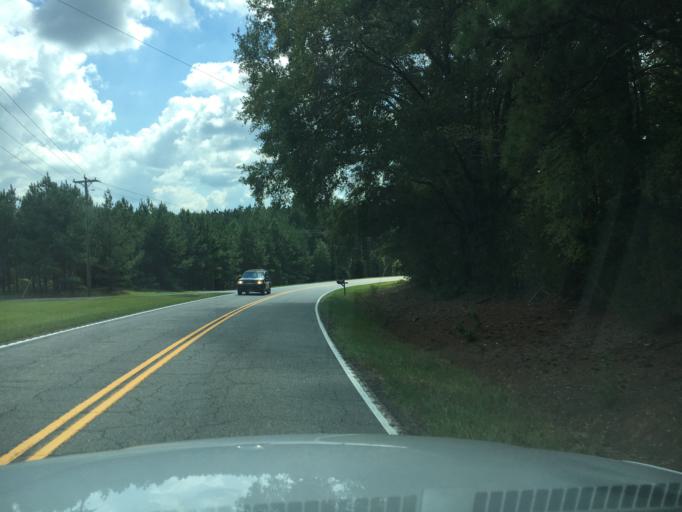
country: US
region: South Carolina
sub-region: Greenwood County
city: Greenwood
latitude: 34.1163
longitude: -82.1265
